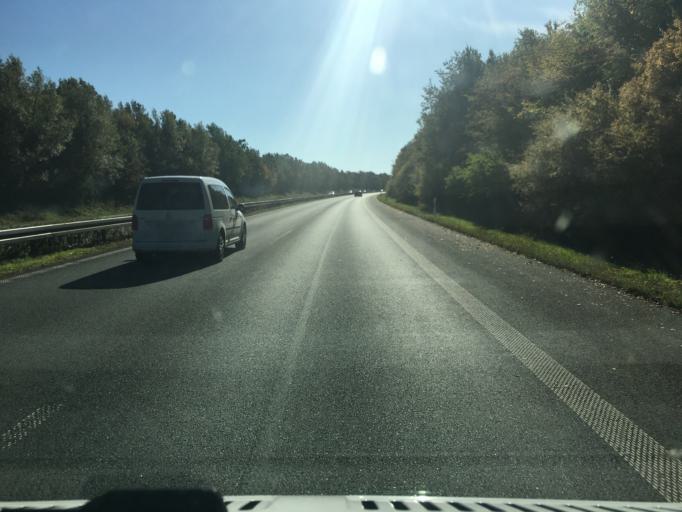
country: DE
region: Saxony
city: Dennheritz
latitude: 50.8055
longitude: 12.4546
